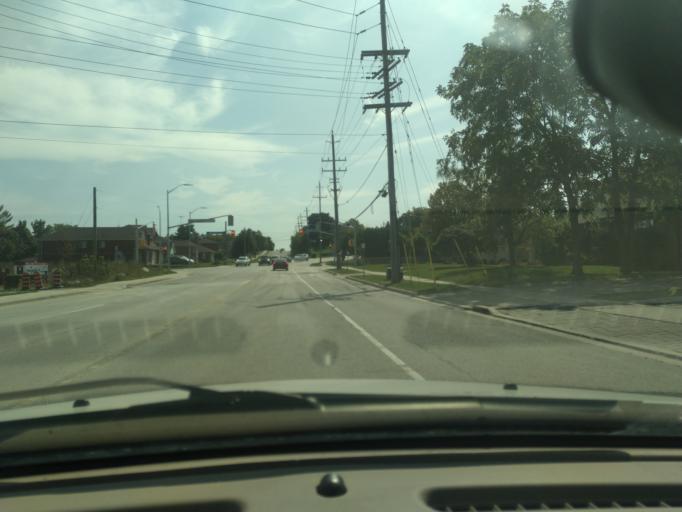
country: CA
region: Ontario
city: Bradford West Gwillimbury
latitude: 44.1106
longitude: -79.5638
